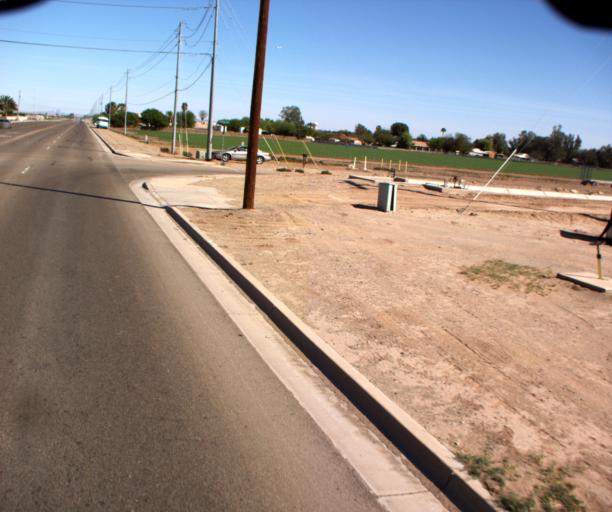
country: US
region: Arizona
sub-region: Yuma County
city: Somerton
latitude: 32.6399
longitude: -114.6500
